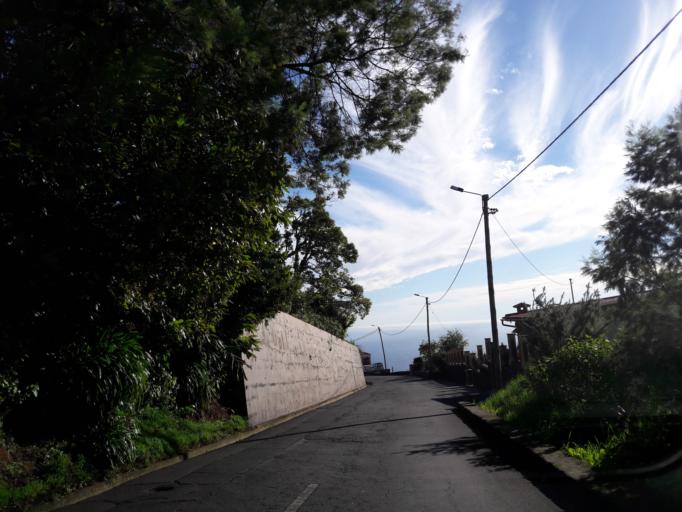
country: PT
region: Madeira
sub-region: Funchal
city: Nossa Senhora do Monte
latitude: 32.6778
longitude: -16.9115
